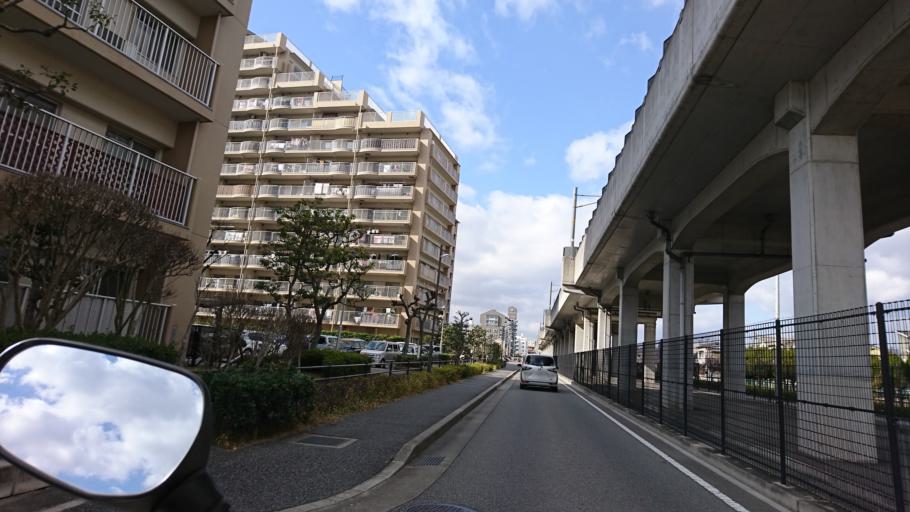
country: JP
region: Hyogo
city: Kakogawacho-honmachi
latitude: 34.7618
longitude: 134.8471
